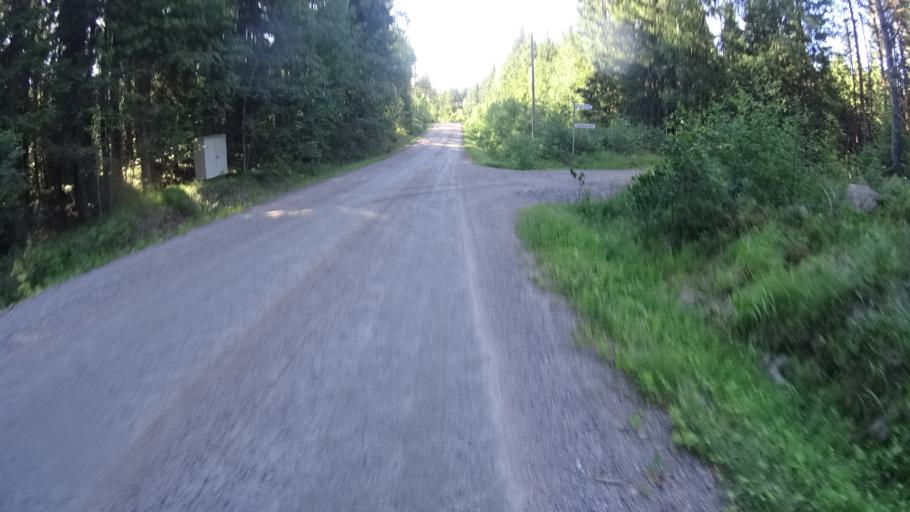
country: FI
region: Uusimaa
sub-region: Helsinki
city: Karkkila
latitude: 60.6504
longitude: 24.1255
